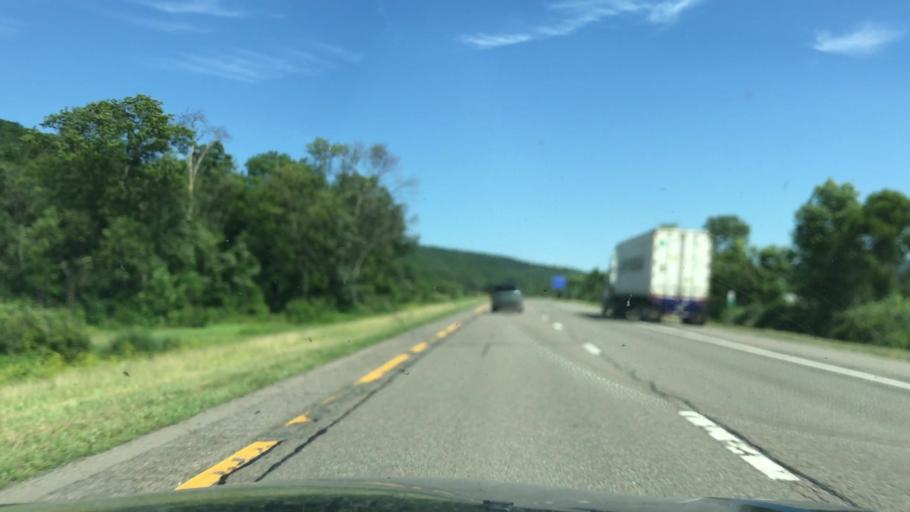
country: US
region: New York
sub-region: Steuben County
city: Painted Post
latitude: 42.1830
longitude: -77.1268
